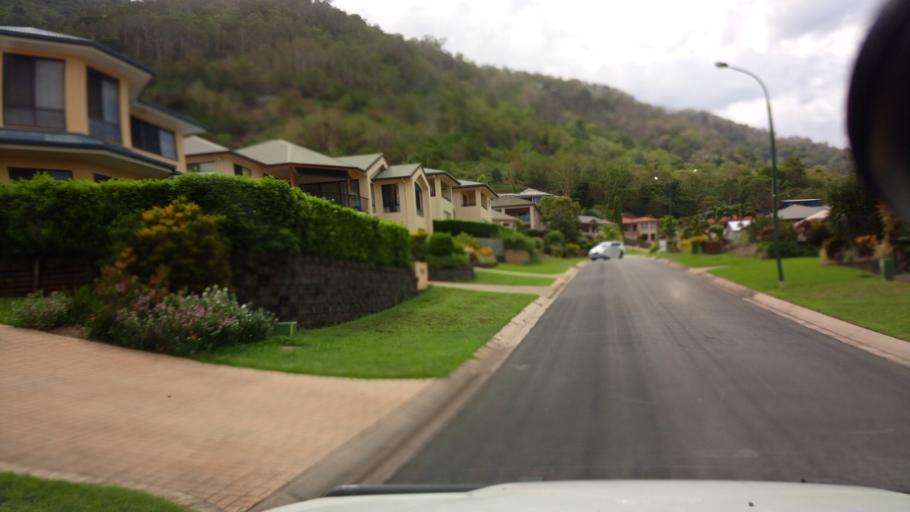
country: AU
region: Queensland
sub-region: Cairns
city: Woree
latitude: -16.9283
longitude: 145.7246
